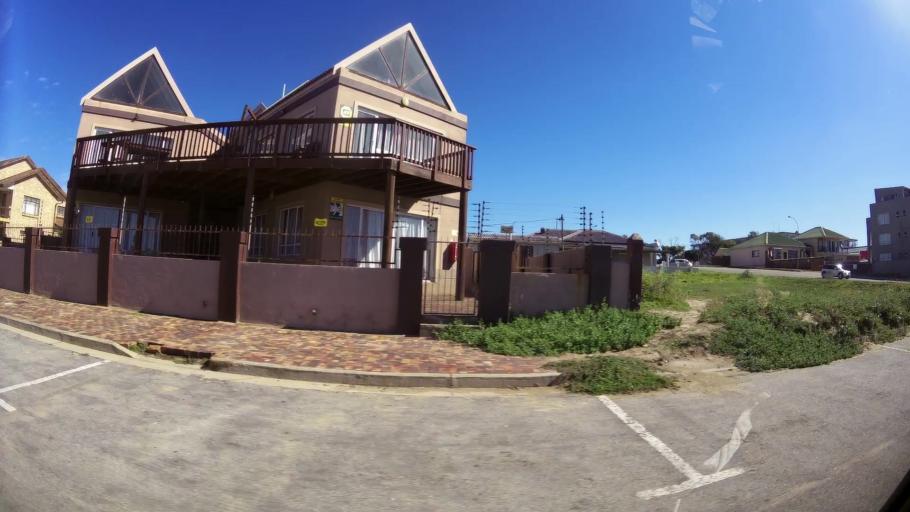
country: ZA
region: Eastern Cape
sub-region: Cacadu District Municipality
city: Jeffrey's Bay
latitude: -34.0554
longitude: 24.9234
